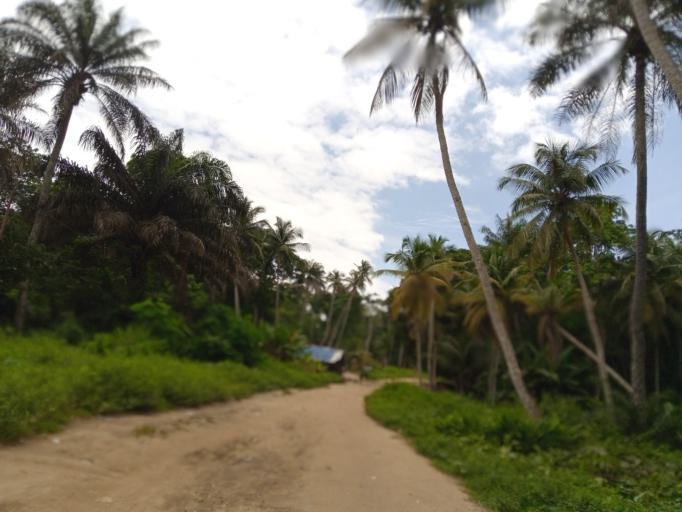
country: SL
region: Northern Province
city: Masoyila
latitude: 8.5595
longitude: -13.1699
